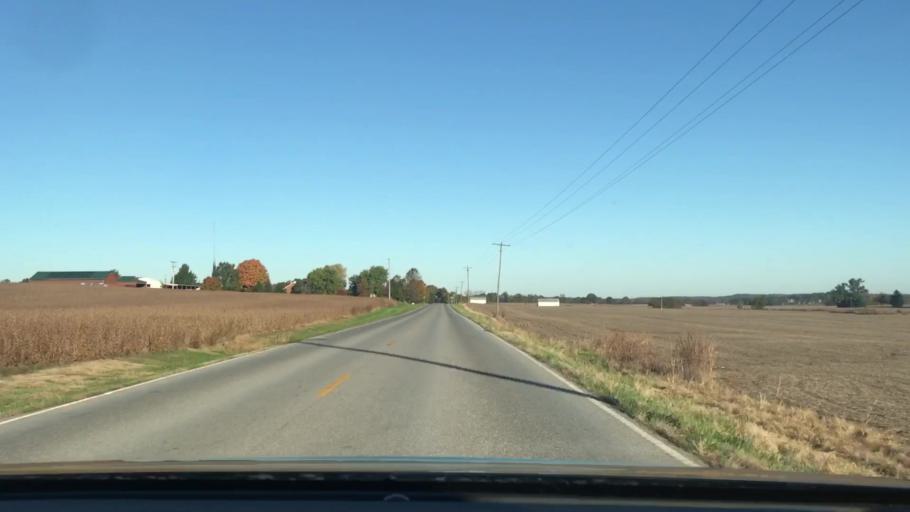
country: US
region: Kentucky
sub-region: Logan County
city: Auburn
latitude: 36.8379
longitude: -86.6901
